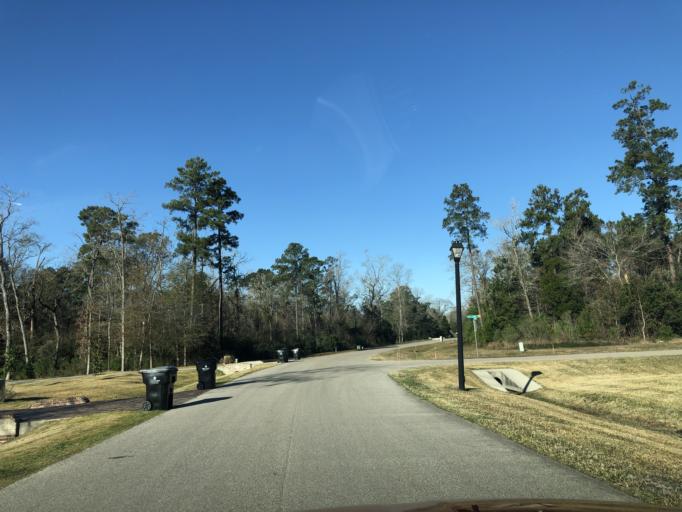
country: US
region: Texas
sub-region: Montgomery County
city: Porter Heights
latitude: 30.0687
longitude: -95.3274
